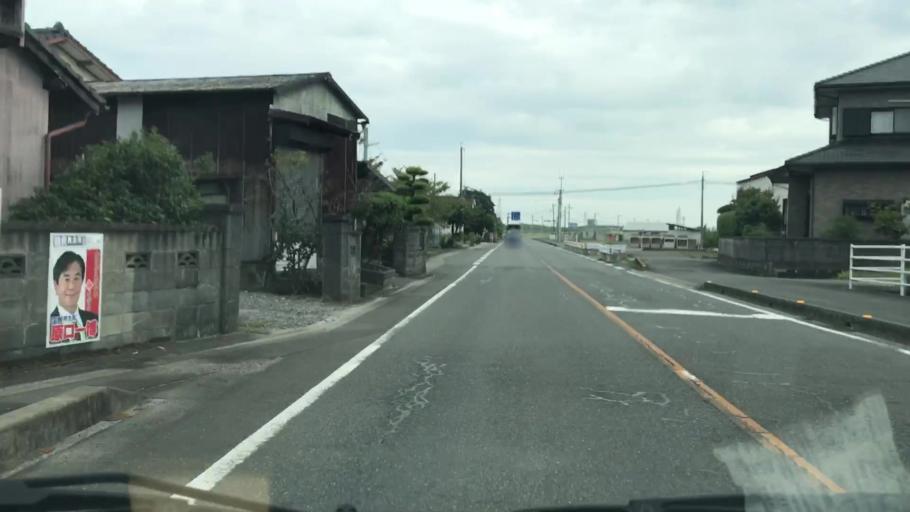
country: JP
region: Saga Prefecture
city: Saga-shi
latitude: 33.2871
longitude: 130.2504
